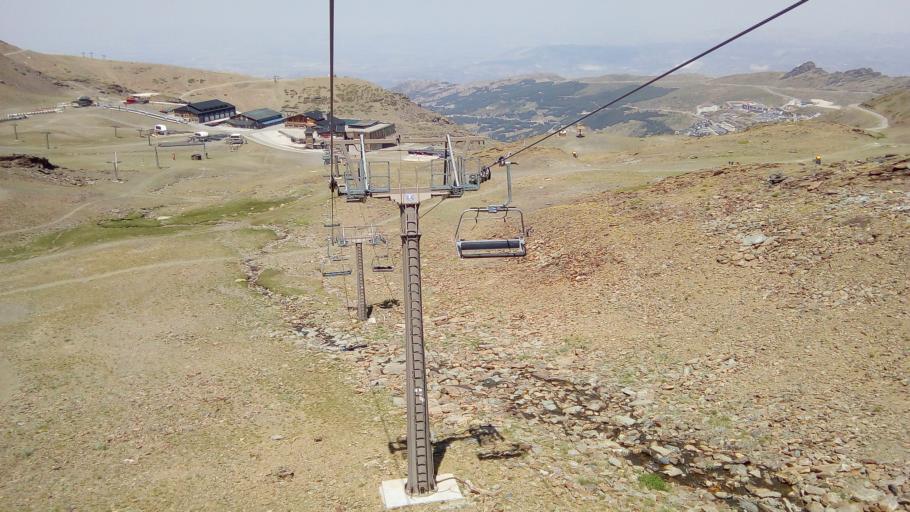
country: ES
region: Andalusia
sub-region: Provincia de Granada
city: Guejar-Sierra
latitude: 37.0682
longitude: -3.3827
